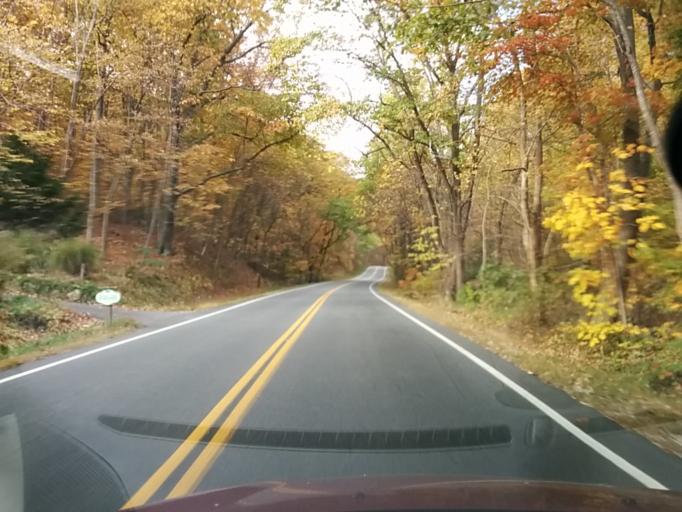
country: US
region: Virginia
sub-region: Nelson County
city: Nellysford
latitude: 37.8917
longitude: -78.9734
